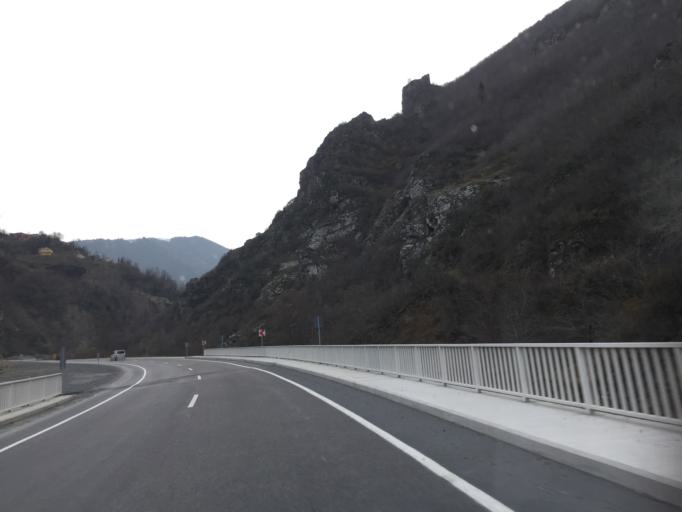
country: TR
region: Trabzon
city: Macka
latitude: 40.7709
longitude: 39.5652
